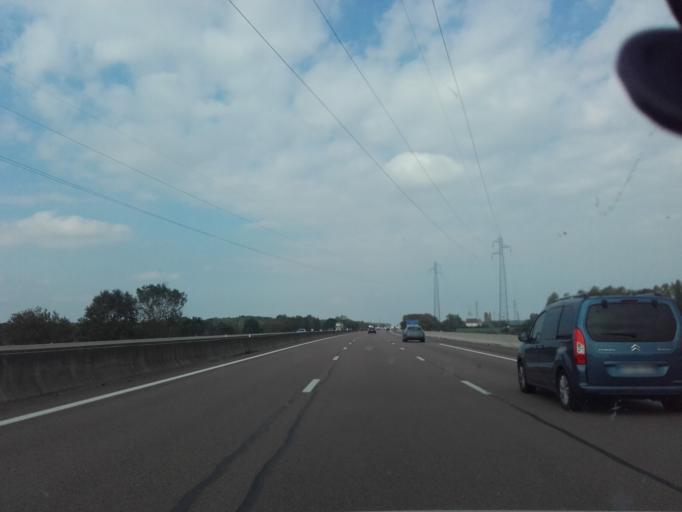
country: FR
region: Bourgogne
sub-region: Departement de Saone-et-Loire
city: Sennecey-le-Grand
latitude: 46.6764
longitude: 4.8467
